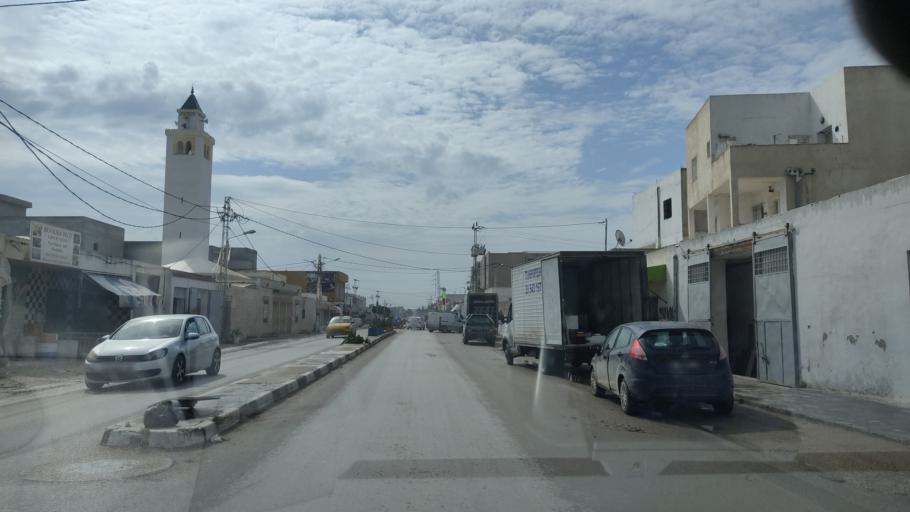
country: TN
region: Ariana
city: Ariana
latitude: 36.8889
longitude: 10.2145
